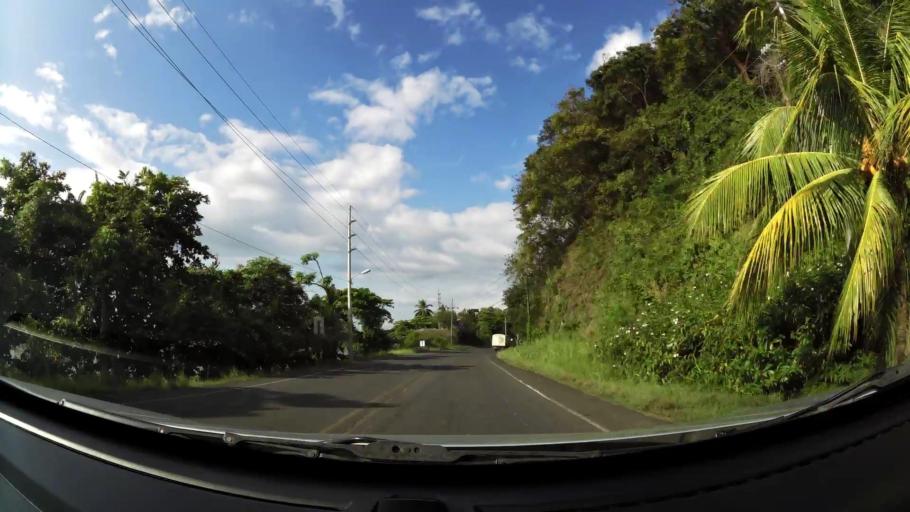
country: CR
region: Puntarenas
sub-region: Canton de Garabito
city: Jaco
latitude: 9.7450
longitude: -84.6306
